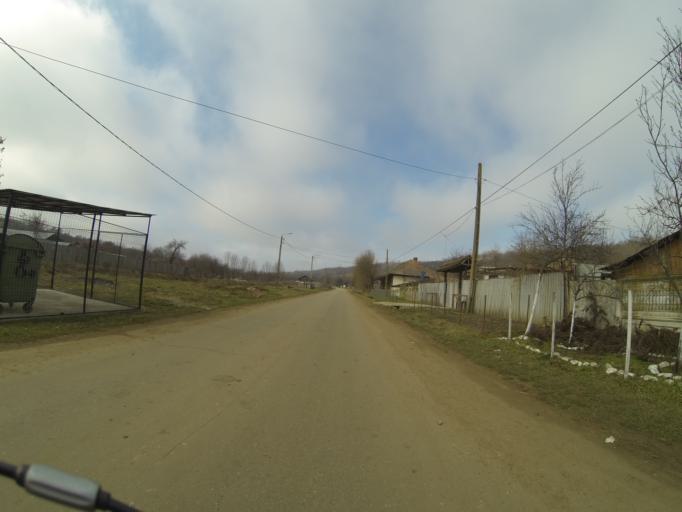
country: RO
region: Mehedinti
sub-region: Comuna Poroina Mare
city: Poroina Mare
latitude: 44.4930
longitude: 22.9985
